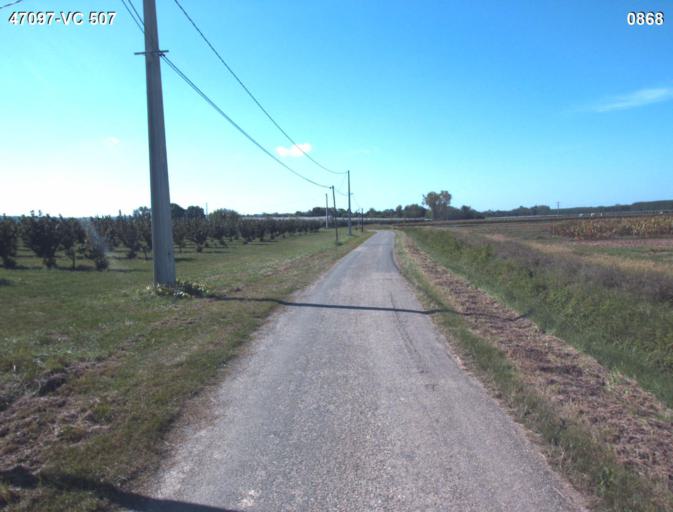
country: FR
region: Aquitaine
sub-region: Departement du Lot-et-Garonne
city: Port-Sainte-Marie
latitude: 44.2428
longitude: 0.3919
